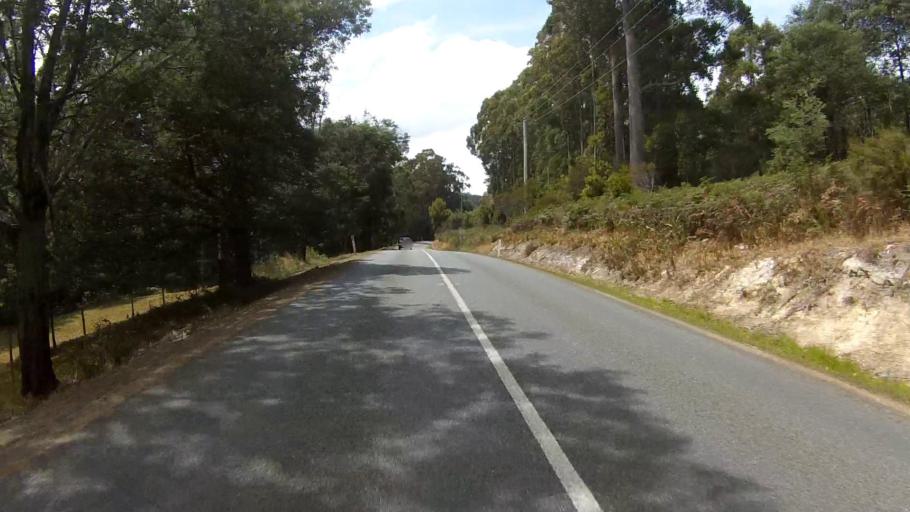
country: AU
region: Tasmania
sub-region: Kingborough
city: Kettering
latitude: -43.1064
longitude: 147.2353
